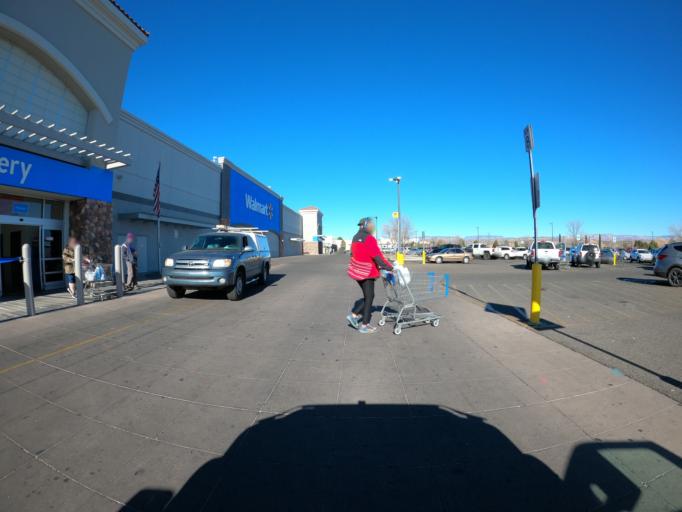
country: US
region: Arizona
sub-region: Yavapai County
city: Verde Village
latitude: 34.7129
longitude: -112.0005
